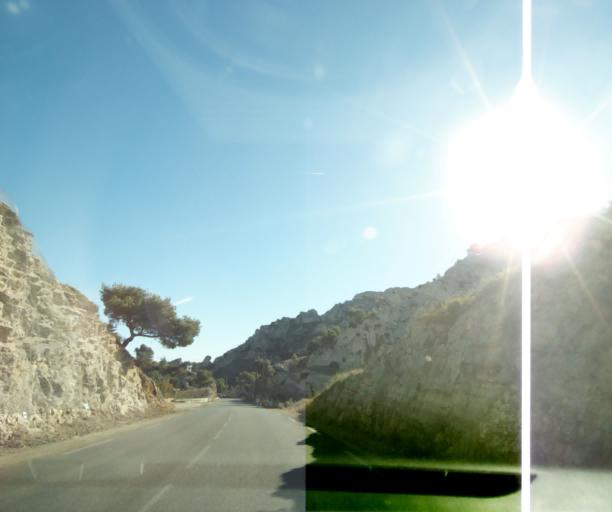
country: FR
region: Provence-Alpes-Cote d'Azur
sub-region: Departement des Bouches-du-Rhone
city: Le Rove
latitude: 43.3612
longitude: 5.2713
